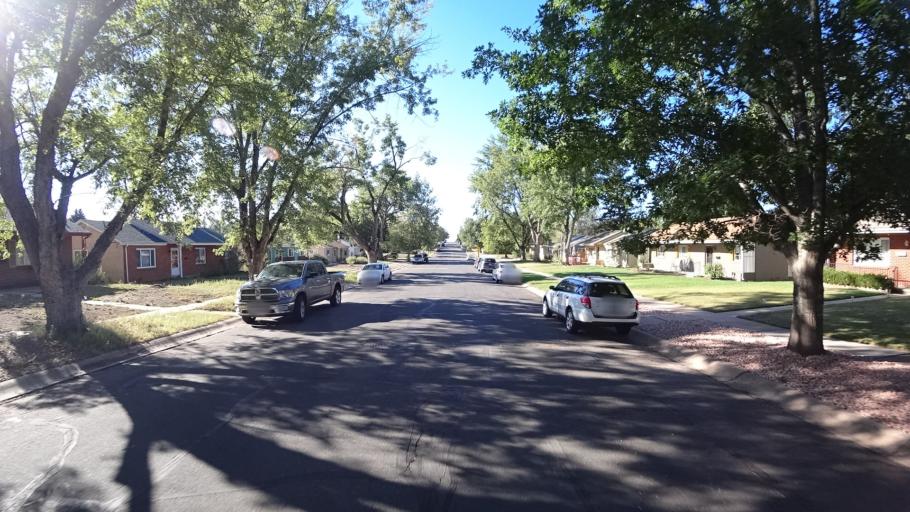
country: US
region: Colorado
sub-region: El Paso County
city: Colorado Springs
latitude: 38.8670
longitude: -104.7954
